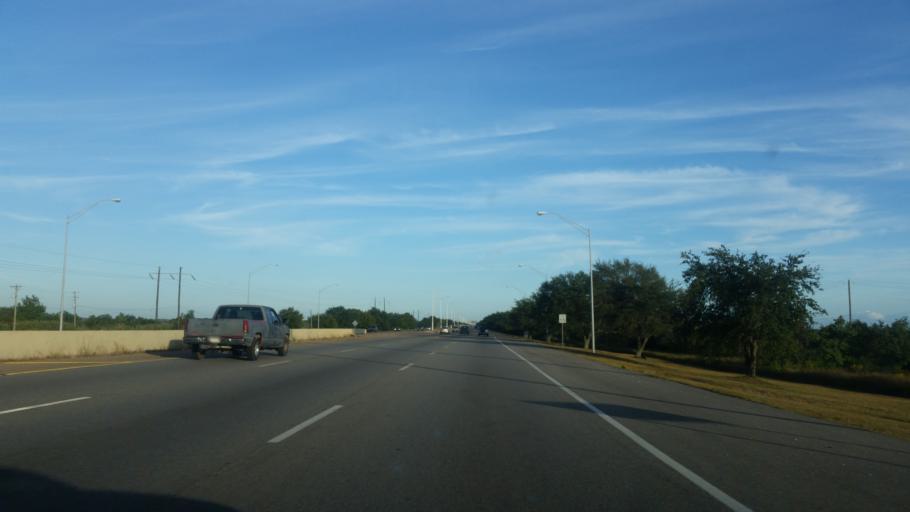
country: US
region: Mississippi
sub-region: Jackson County
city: Gautier
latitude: 30.3819
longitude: -88.6047
